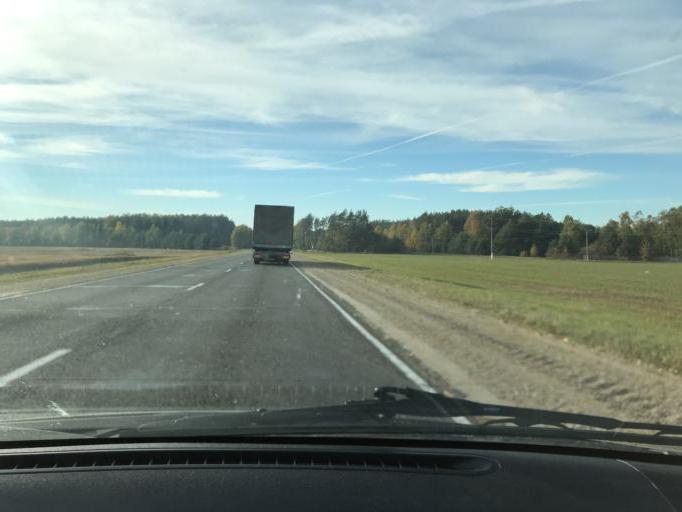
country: BY
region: Brest
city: Horad Pinsk
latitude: 52.1504
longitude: 25.8582
